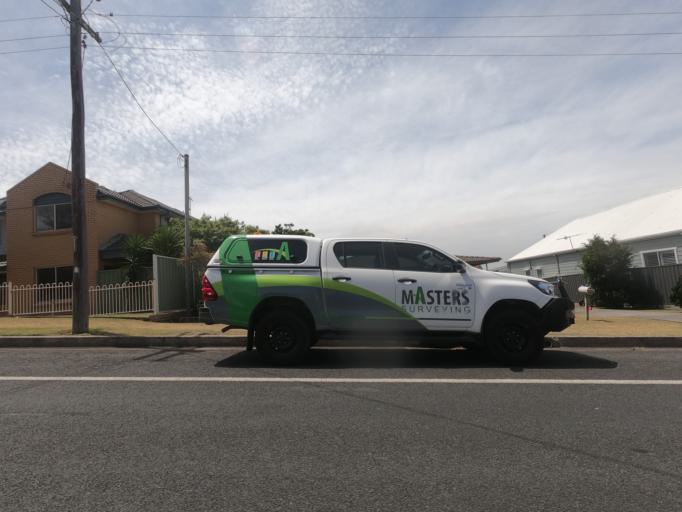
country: AU
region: New South Wales
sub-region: Wollongong
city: Mount Ousley
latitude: -34.3897
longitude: 150.8782
